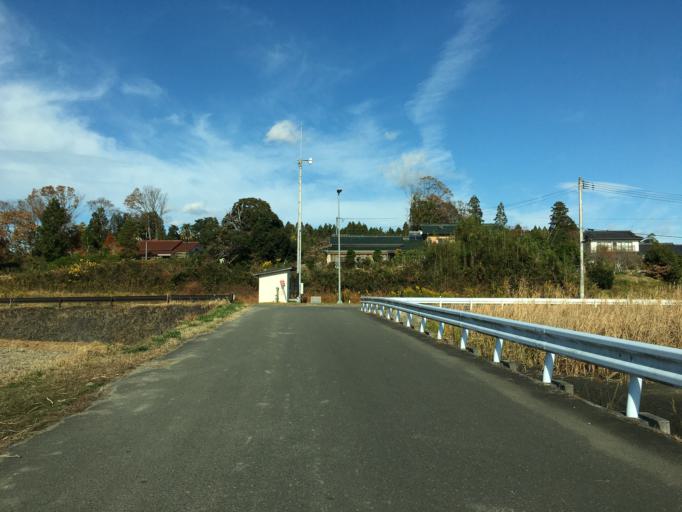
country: JP
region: Miyagi
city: Marumori
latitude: 37.8950
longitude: 140.9206
